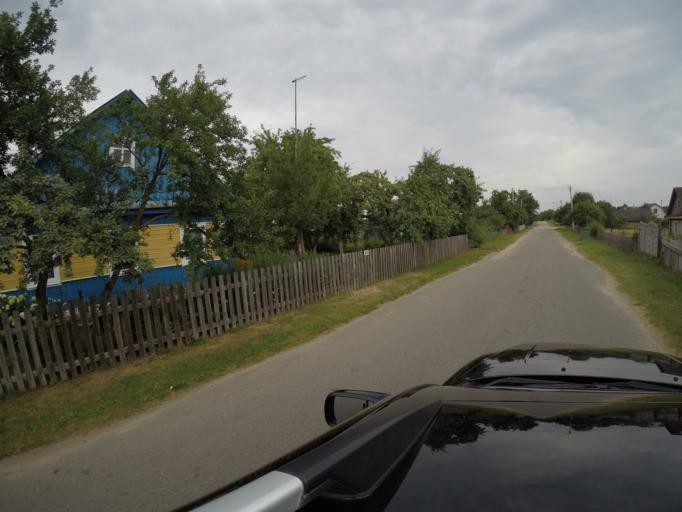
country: BY
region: Grodnenskaya
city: Hal'shany
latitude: 54.2585
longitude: 26.0188
